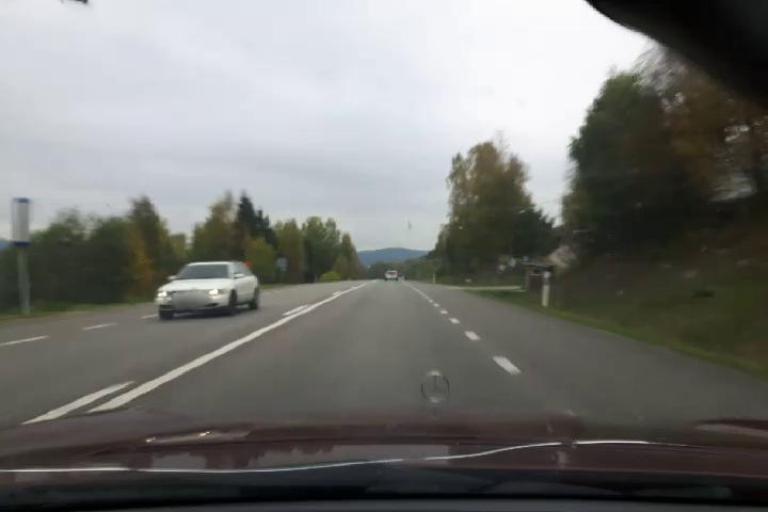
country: SE
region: Vaesternorrland
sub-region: Kramfors Kommun
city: Nordingra
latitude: 63.0180
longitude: 18.2946
